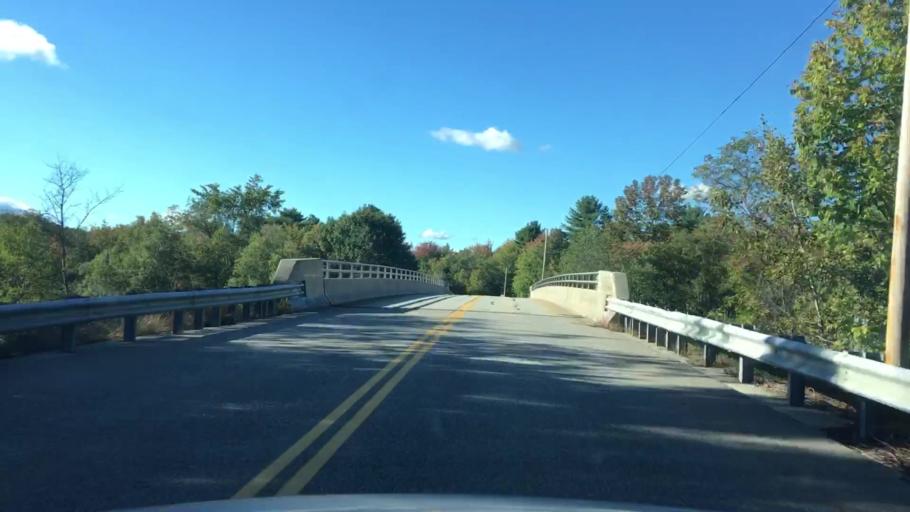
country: US
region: Maine
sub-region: Androscoggin County
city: Lisbon
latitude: 44.0705
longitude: -70.1383
